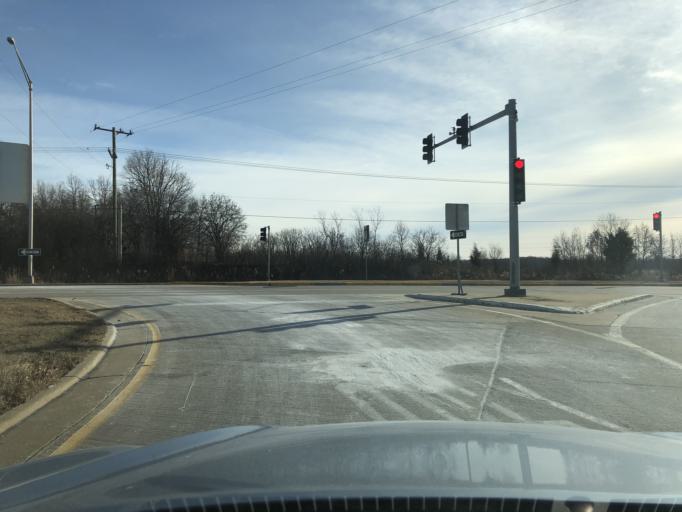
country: US
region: Illinois
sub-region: Lake County
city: Gurnee
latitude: 42.3566
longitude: -87.9360
